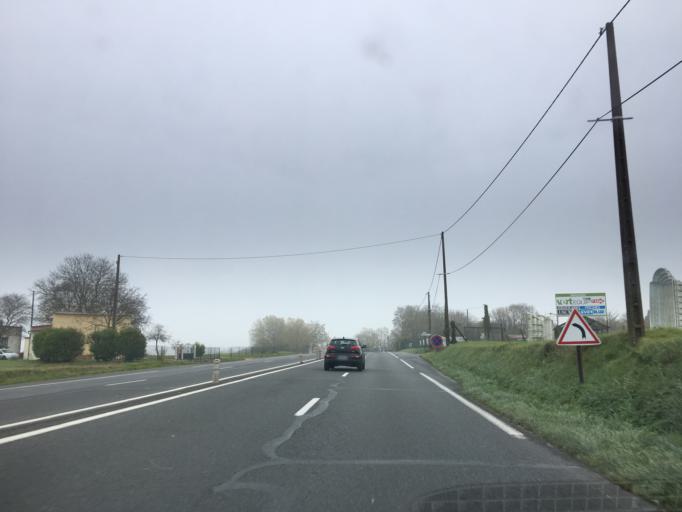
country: FR
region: Ile-de-France
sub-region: Departement de Seine-et-Marne
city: Vernou-la-Celle-sur-Seine
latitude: 48.3622
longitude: 2.8617
